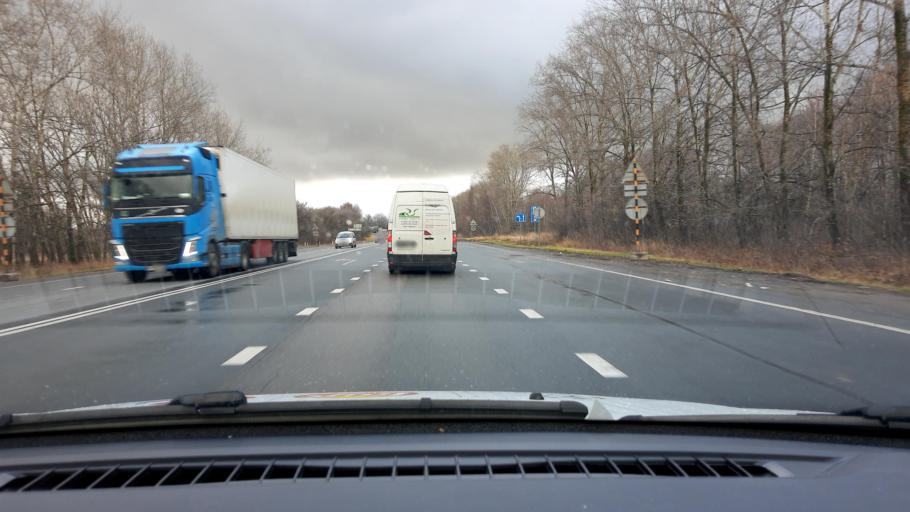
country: RU
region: Nizjnij Novgorod
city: Pamyat' Parizhskoy Kommuny
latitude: 55.9997
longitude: 44.6376
